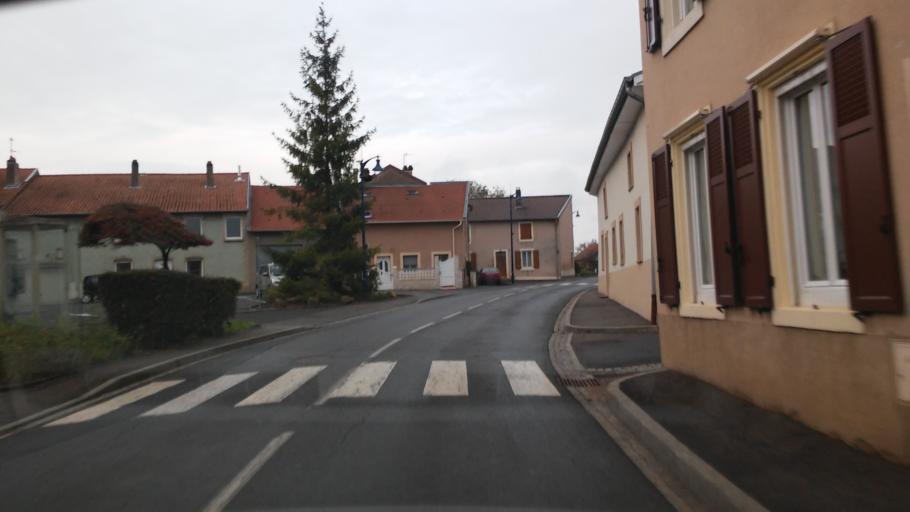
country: FR
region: Lorraine
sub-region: Departement de la Moselle
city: Ennery
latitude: 49.2077
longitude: 6.2346
